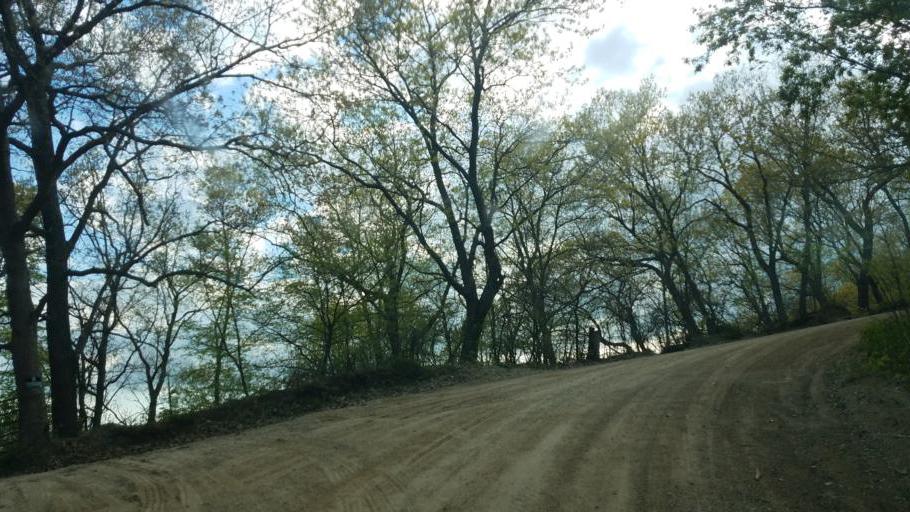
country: US
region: Wisconsin
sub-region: Vernon County
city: Hillsboro
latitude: 43.6456
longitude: -90.3820
